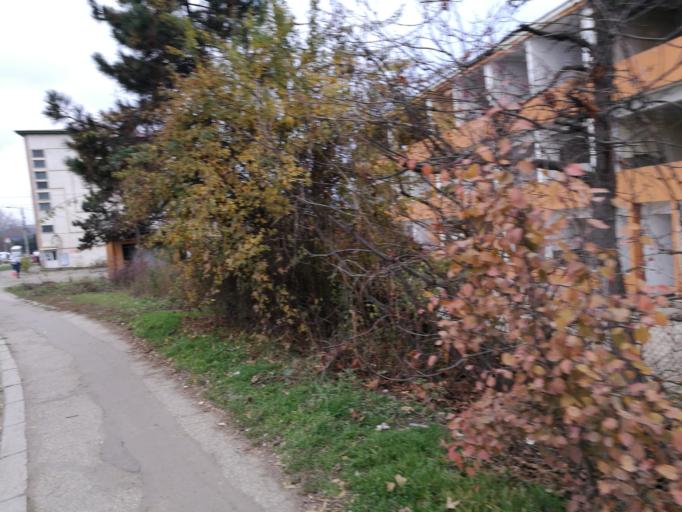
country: RO
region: Suceava
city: Suceava
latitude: 47.6663
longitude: 26.2704
